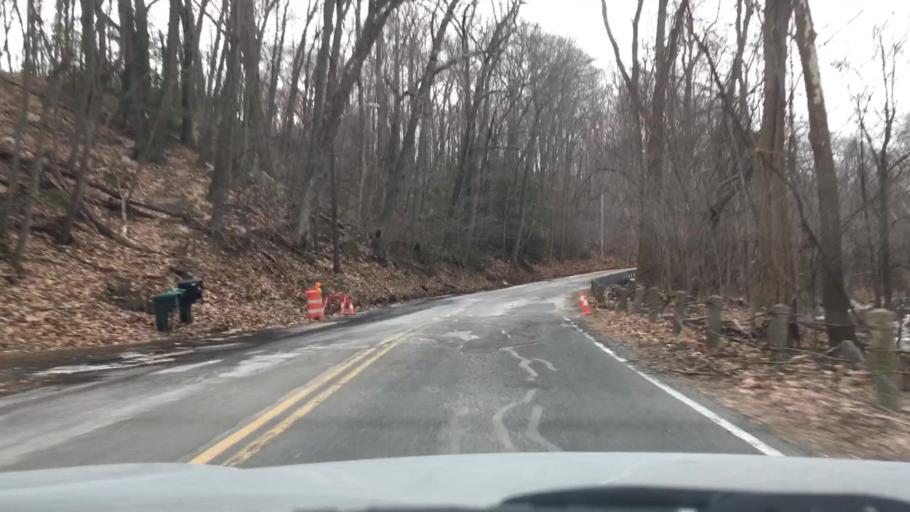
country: US
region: Massachusetts
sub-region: Hampshire County
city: Northampton
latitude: 42.3260
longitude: -72.6678
